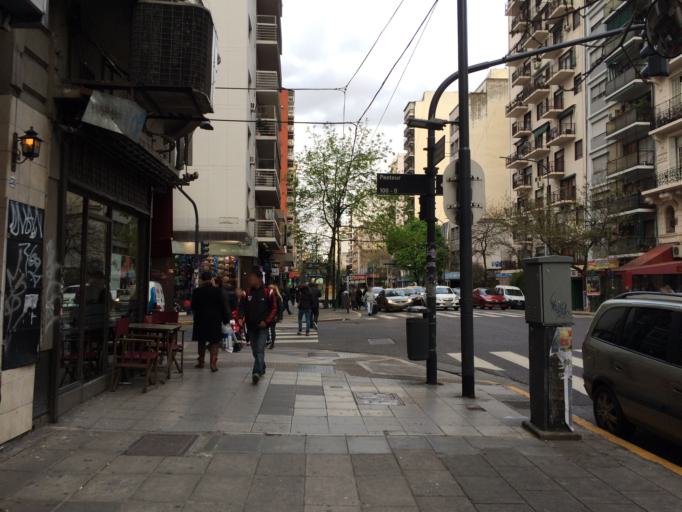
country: AR
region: Buenos Aires F.D.
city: Buenos Aires
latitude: -34.6097
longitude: -58.3994
